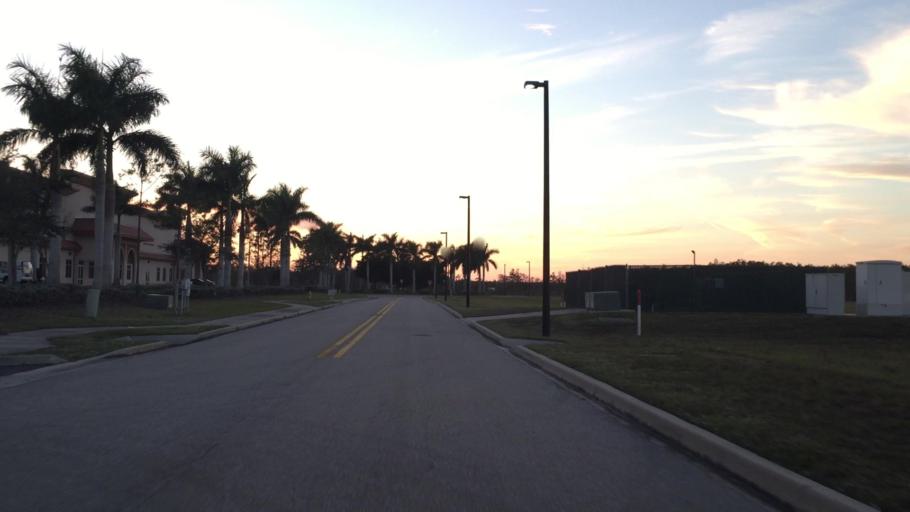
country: US
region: Florida
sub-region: Lee County
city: Three Oaks
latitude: 26.5297
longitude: -81.7883
